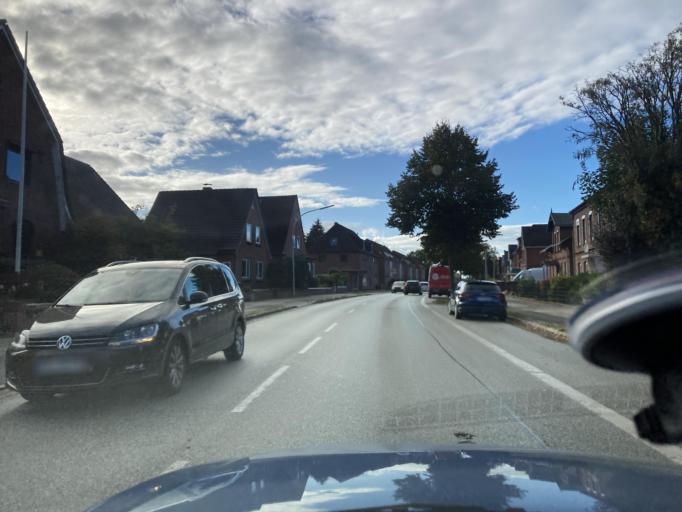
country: DE
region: Schleswig-Holstein
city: Rendsburg
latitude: 54.3078
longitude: 9.6468
